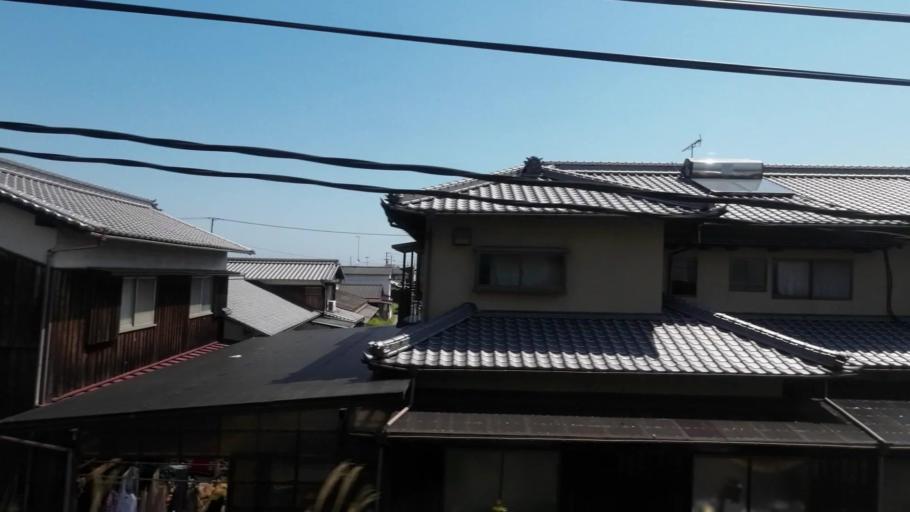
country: JP
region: Ehime
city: Saijo
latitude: 33.9372
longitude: 133.0789
